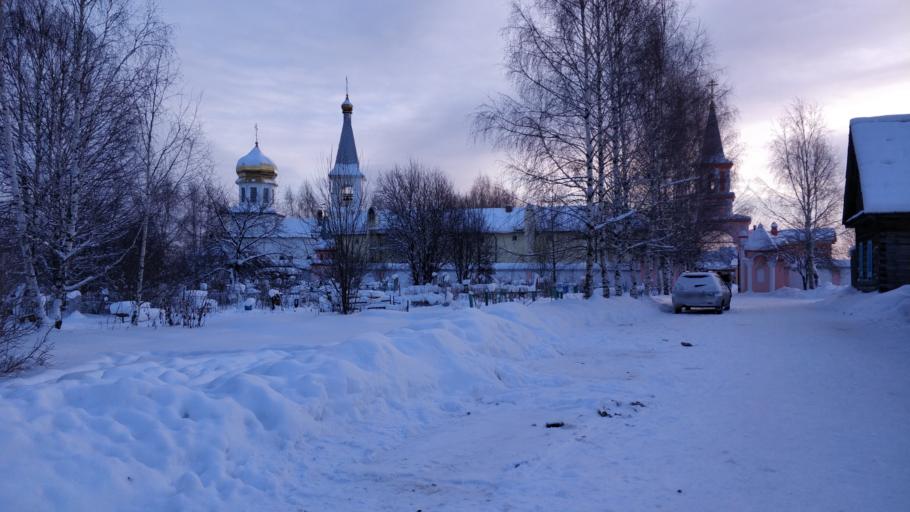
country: RU
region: Perm
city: Verkhnechusovskiye Gorodki
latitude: 58.1987
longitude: 57.1384
